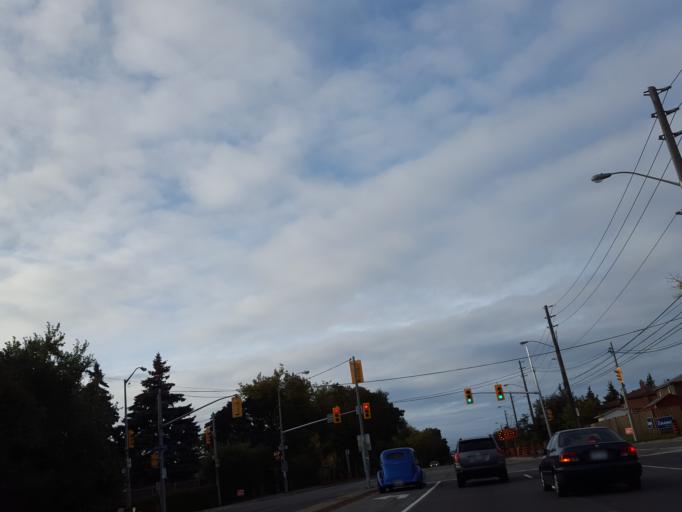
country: CA
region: Ontario
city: Scarborough
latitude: 43.7727
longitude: -79.3051
